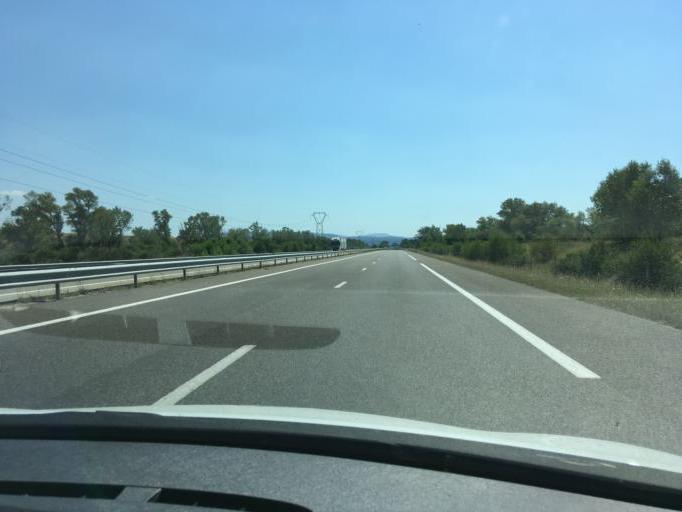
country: FR
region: Provence-Alpes-Cote d'Azur
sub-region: Departement des Alpes-de-Haute-Provence
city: Sainte-Tulle
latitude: 43.7544
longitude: 5.7711
